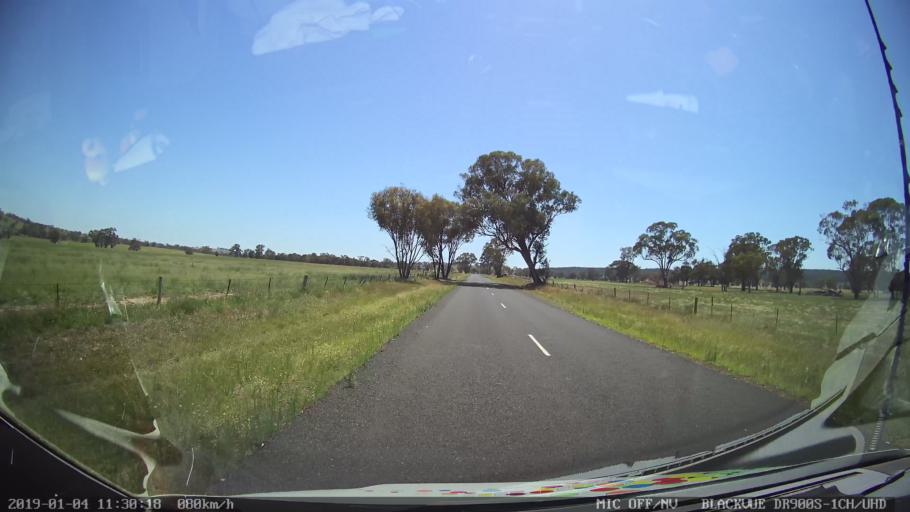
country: AU
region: New South Wales
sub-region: Cabonne
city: Molong
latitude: -33.0789
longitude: 148.7796
